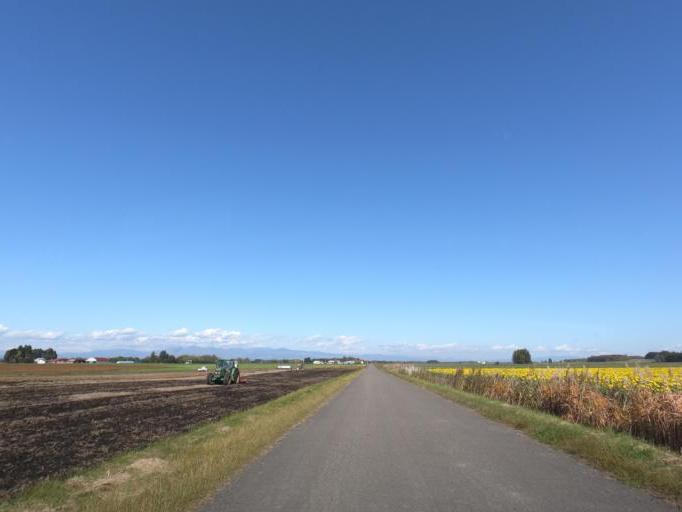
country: JP
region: Hokkaido
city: Otofuke
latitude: 43.0176
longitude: 143.2681
